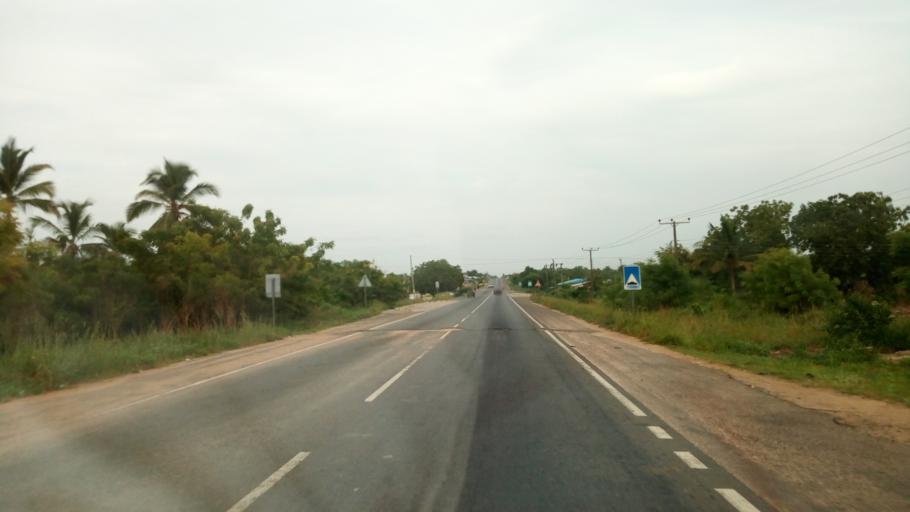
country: GH
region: Volta
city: Keta
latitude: 6.0590
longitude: 0.9933
